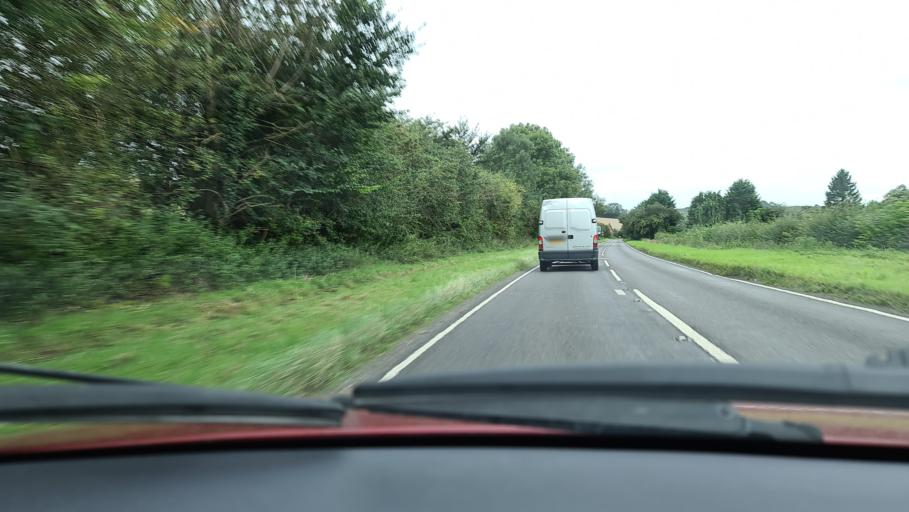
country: GB
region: England
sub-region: Buckinghamshire
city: Chesham
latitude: 51.7000
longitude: -0.6266
